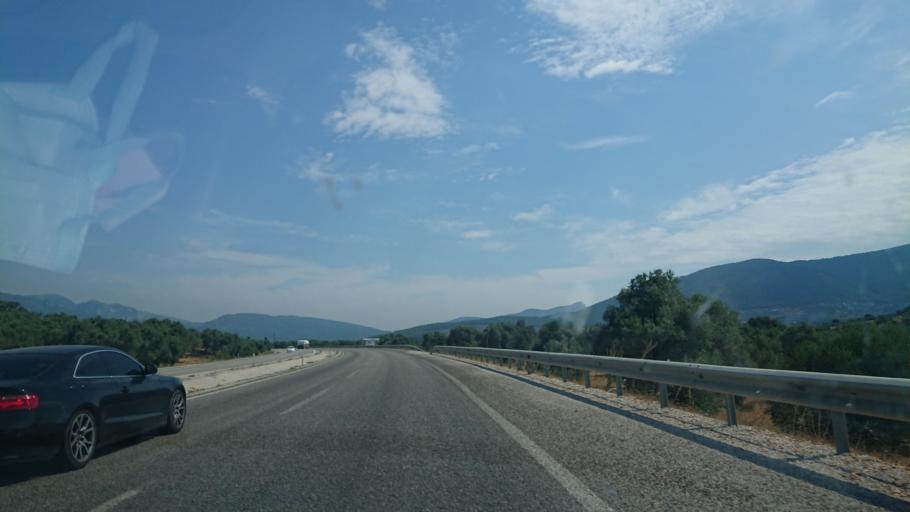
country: TR
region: Izmir
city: Dagkizilca
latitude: 38.2823
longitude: 27.4018
